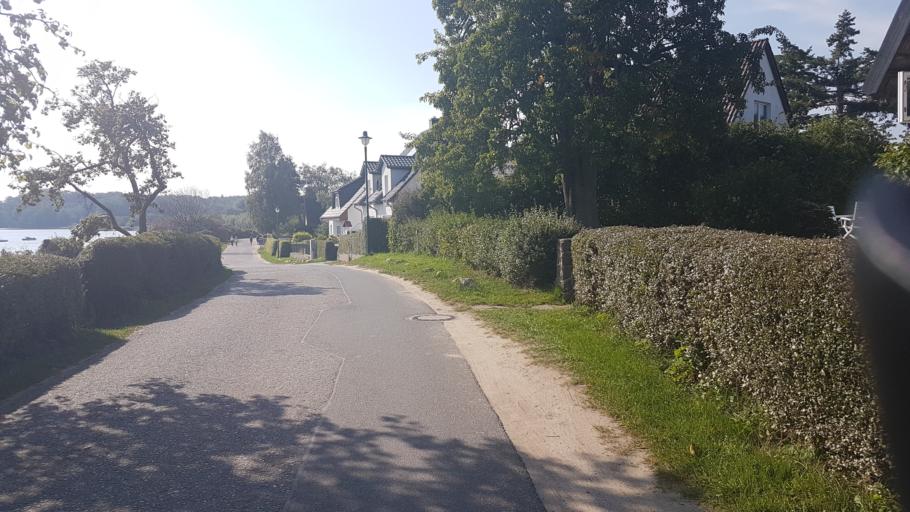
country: DE
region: Mecklenburg-Vorpommern
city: Putbus
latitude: 54.3367
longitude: 13.4880
